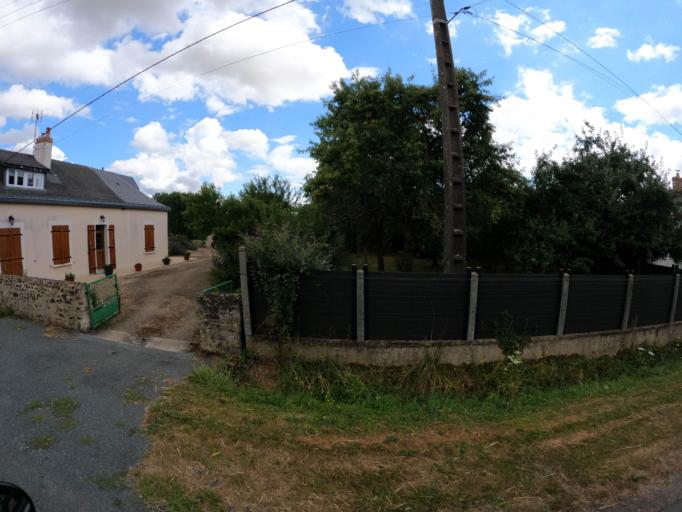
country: FR
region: Pays de la Loire
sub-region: Departement de Maine-et-Loire
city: Mire
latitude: 47.7749
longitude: -0.4727
